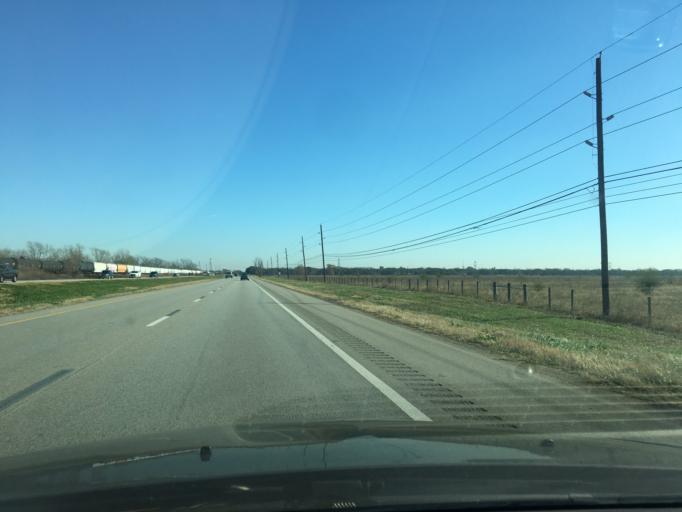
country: US
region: Texas
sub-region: Fort Bend County
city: New Territory
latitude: 29.5991
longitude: -95.7085
